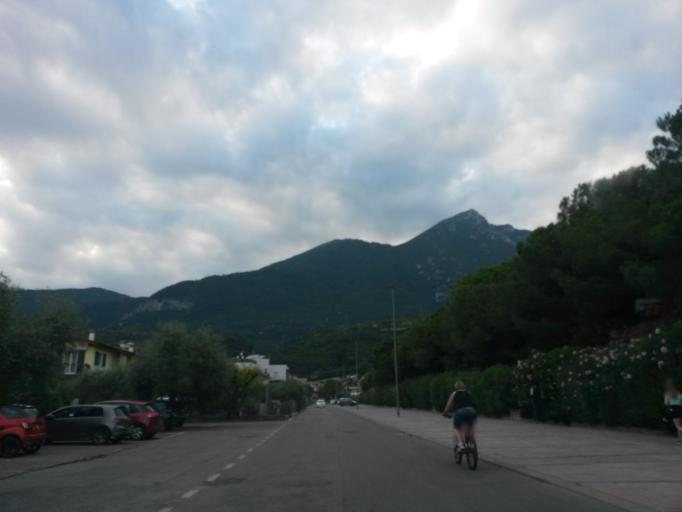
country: IT
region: Lombardy
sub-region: Provincia di Brescia
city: Toscolano Maderno
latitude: 45.6395
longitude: 10.6174
